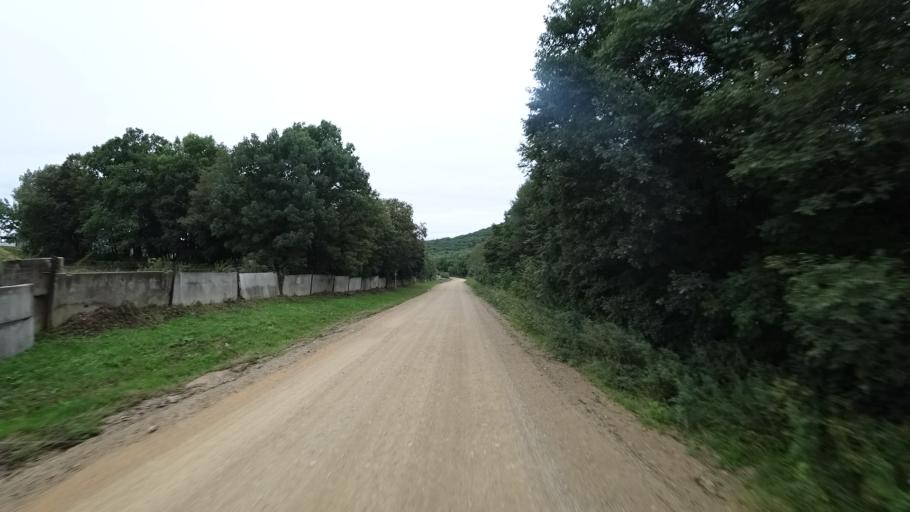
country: RU
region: Primorskiy
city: Rettikhovka
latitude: 44.1758
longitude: 132.8515
